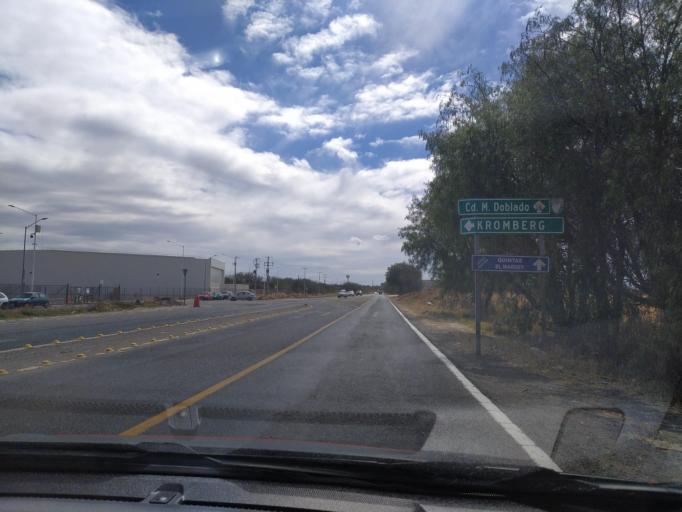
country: LA
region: Oudomxai
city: Muang La
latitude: 21.0042
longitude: 101.8311
